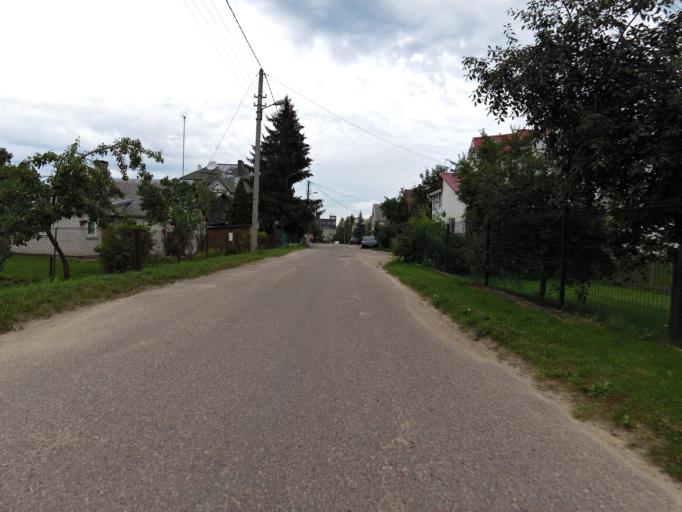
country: LT
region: Vilnius County
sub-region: Vilnius
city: Vilnius
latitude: 54.7089
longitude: 25.2755
